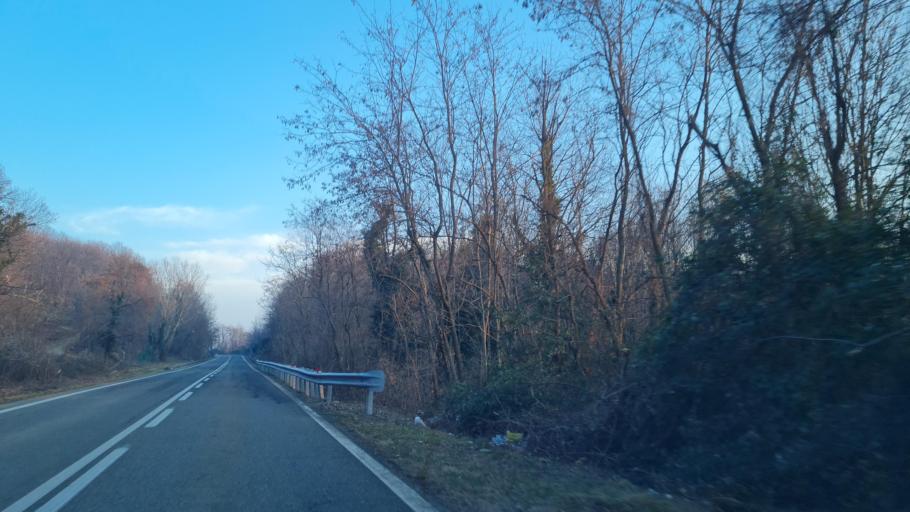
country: IT
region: Piedmont
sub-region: Provincia di Torino
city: Andrate
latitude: 45.5165
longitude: 7.8856
